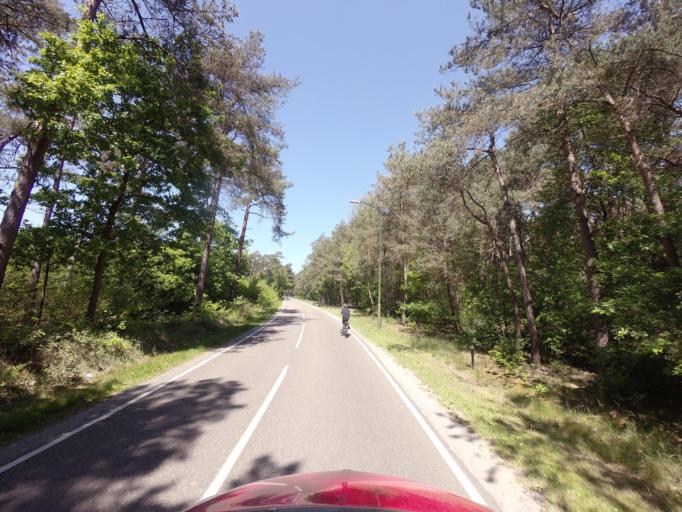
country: NL
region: North Brabant
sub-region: Bergeijk
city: Bergeyk
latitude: 51.2983
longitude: 5.3022
